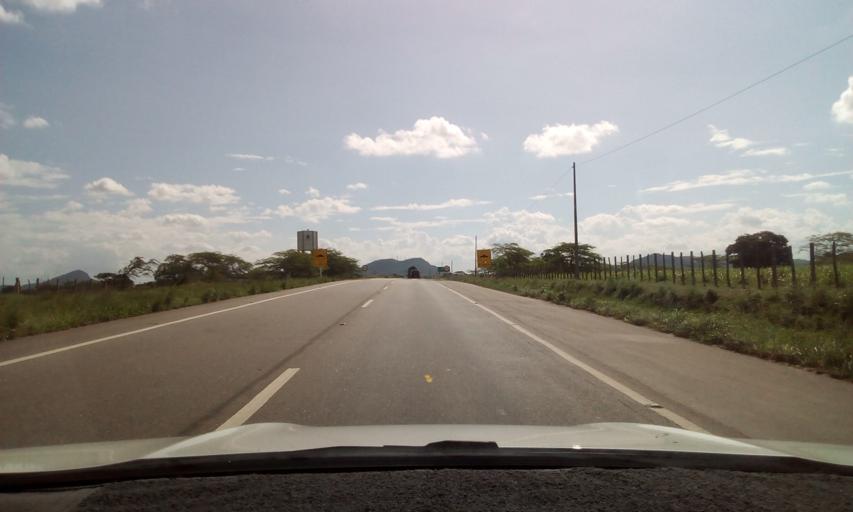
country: BR
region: Paraiba
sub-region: Gurinhem
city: Gurinhem
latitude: -7.1646
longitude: -35.3519
